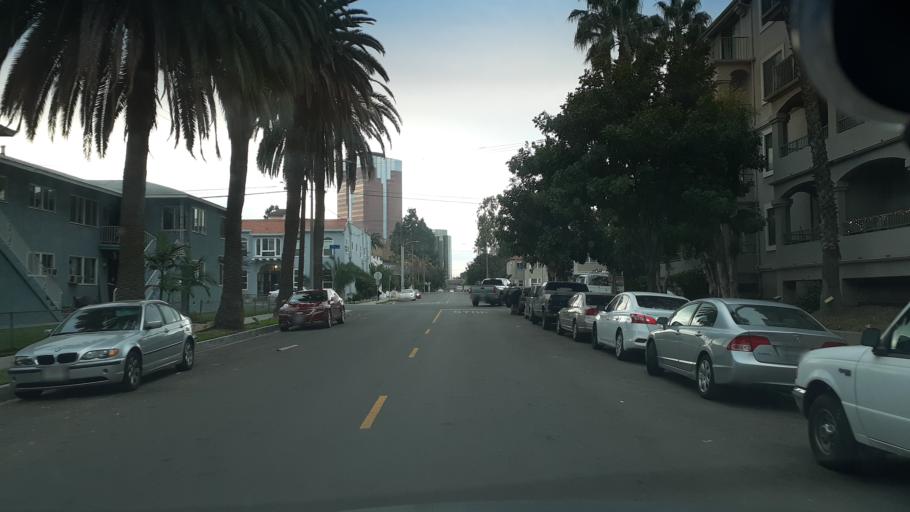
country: US
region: California
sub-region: Los Angeles County
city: Long Beach
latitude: 33.7735
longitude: -118.2006
